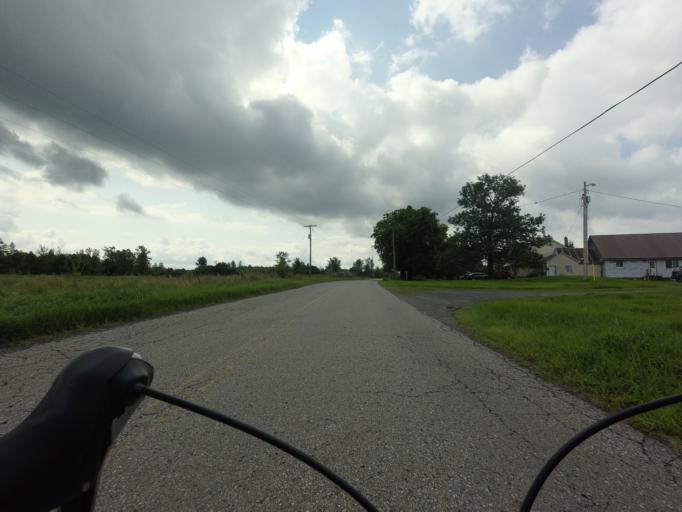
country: CA
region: Ontario
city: Brockville
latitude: 44.7889
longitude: -75.7207
